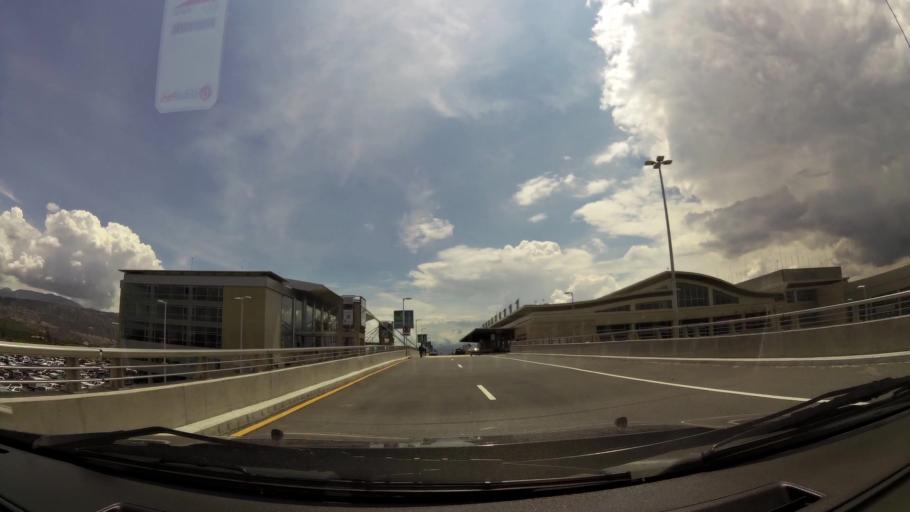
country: EC
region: Pichincha
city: Quito
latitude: -0.1253
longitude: -78.3609
